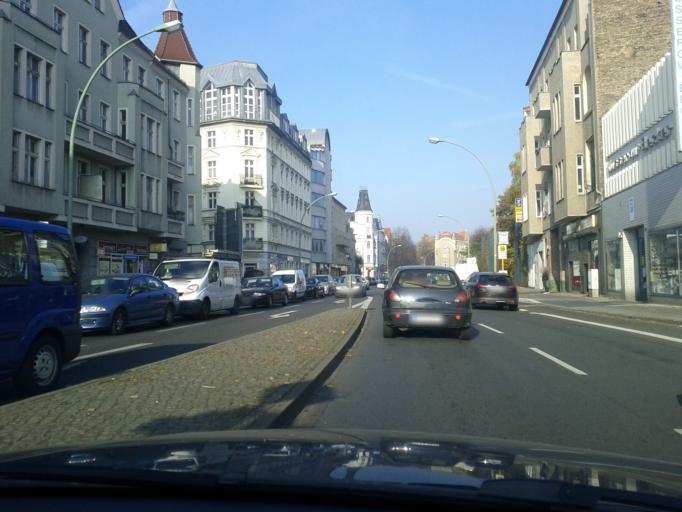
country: DE
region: Berlin
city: Britz
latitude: 52.4639
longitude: 13.4440
